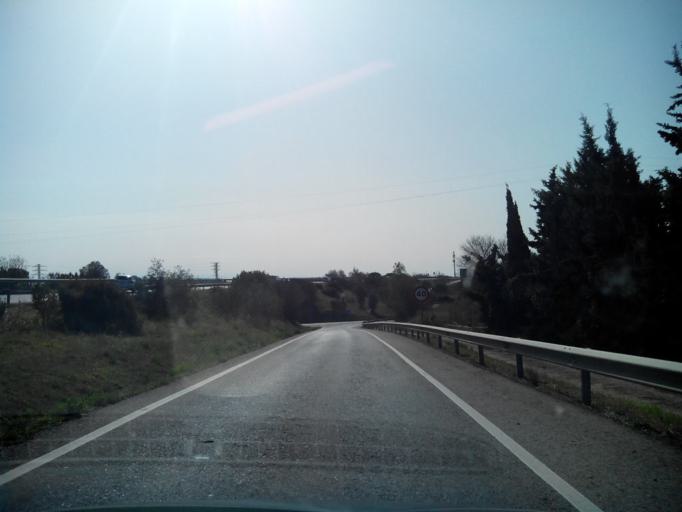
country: ES
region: Catalonia
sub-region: Provincia de Tarragona
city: Alcover
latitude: 41.2645
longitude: 1.1762
